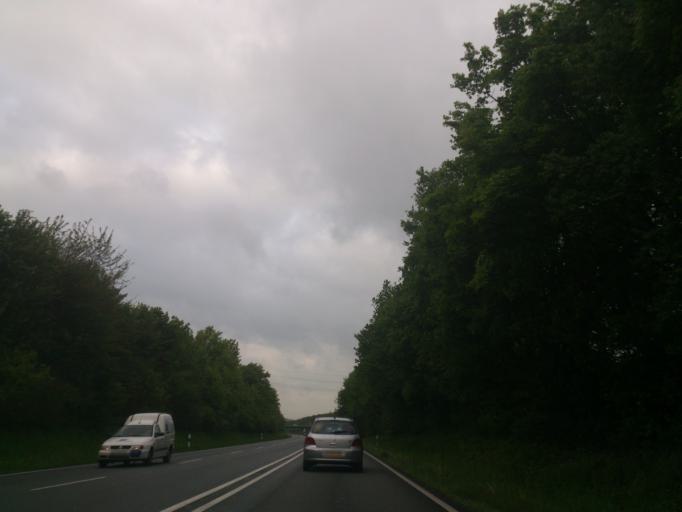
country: DE
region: North Rhine-Westphalia
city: Bad Lippspringe
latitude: 51.7179
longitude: 8.8243
